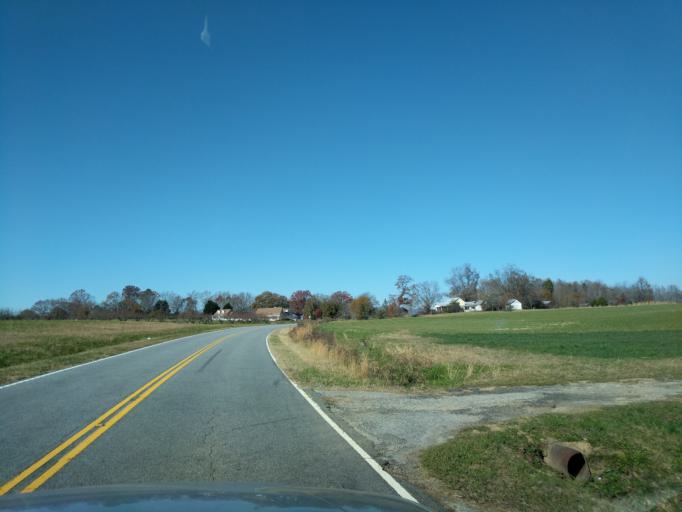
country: US
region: South Carolina
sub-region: Spartanburg County
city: Landrum
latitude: 35.0845
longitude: -82.2154
